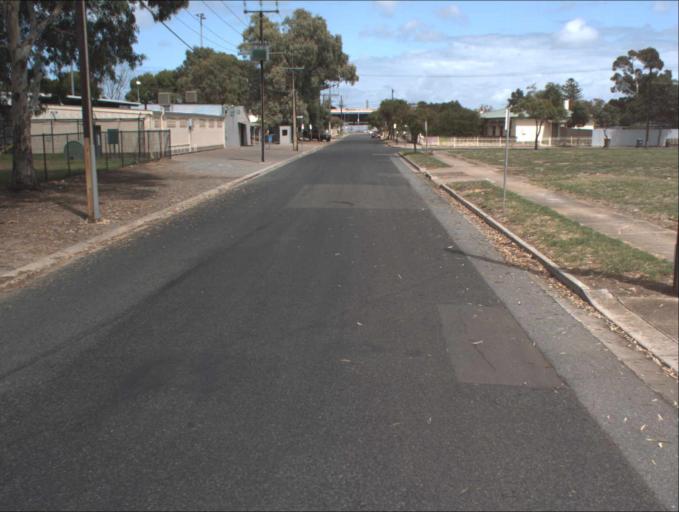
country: AU
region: South Australia
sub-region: Port Adelaide Enfield
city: Enfield
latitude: -34.8506
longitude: 138.5944
